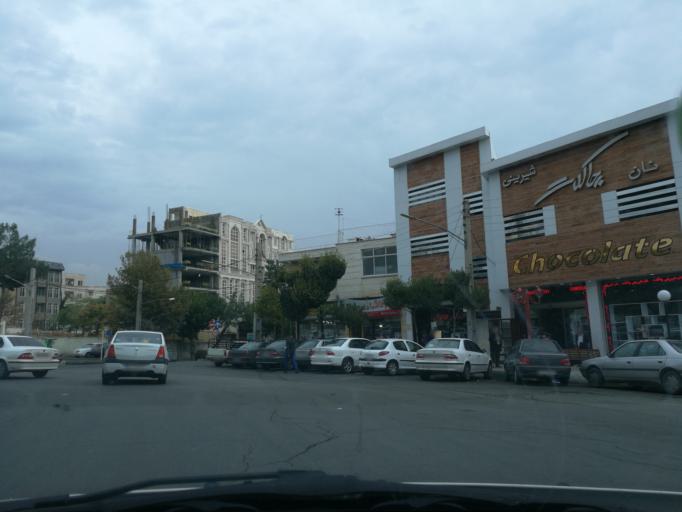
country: IR
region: Alborz
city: Karaj
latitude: 35.8498
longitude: 50.9672
